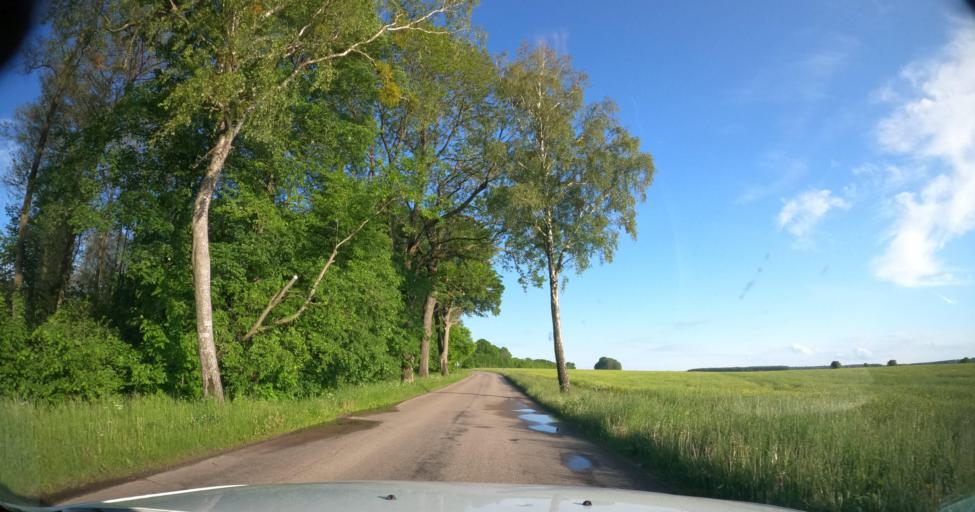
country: PL
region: Warmian-Masurian Voivodeship
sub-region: Powiat braniewski
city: Braniewo
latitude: 54.2833
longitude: 19.8953
